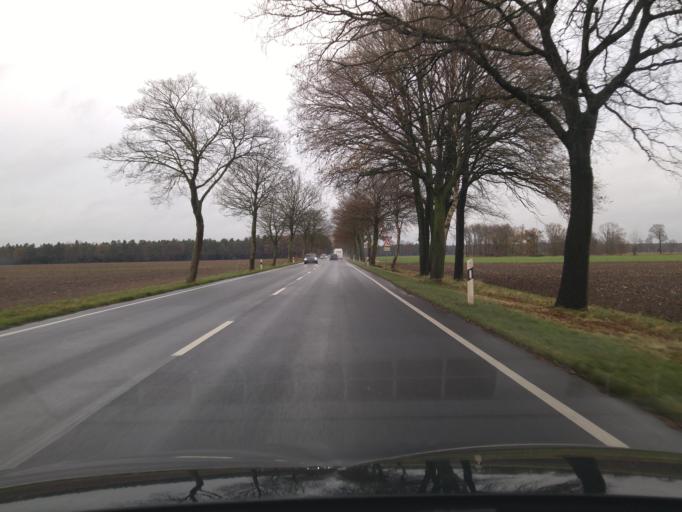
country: DE
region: Lower Saxony
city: Gross Oesingen
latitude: 52.6671
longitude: 10.4674
